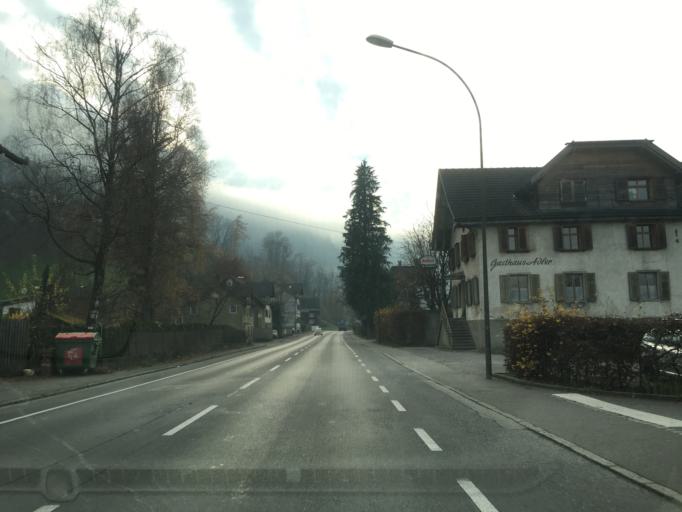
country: AT
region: Vorarlberg
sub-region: Politischer Bezirk Dornbirn
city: Hohenems
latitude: 47.3511
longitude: 9.6768
